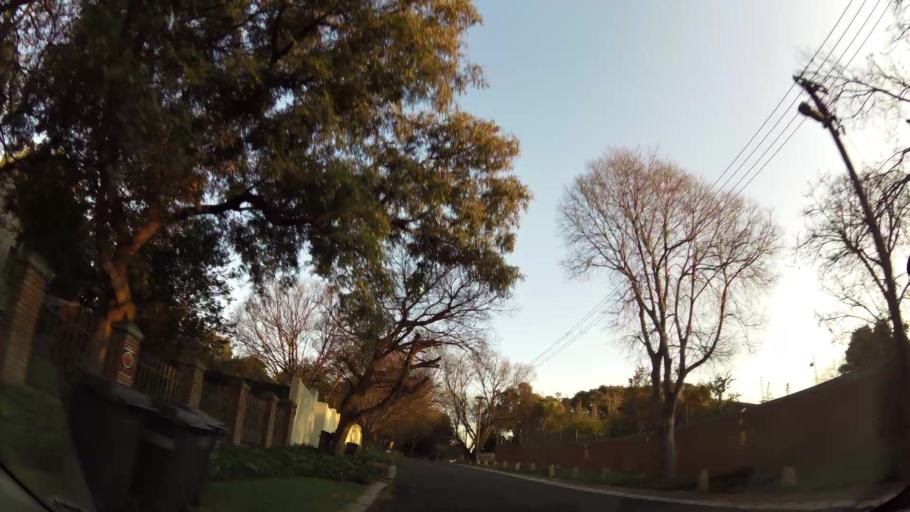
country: ZA
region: Gauteng
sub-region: City of Johannesburg Metropolitan Municipality
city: Johannesburg
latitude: -26.1073
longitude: 27.9976
